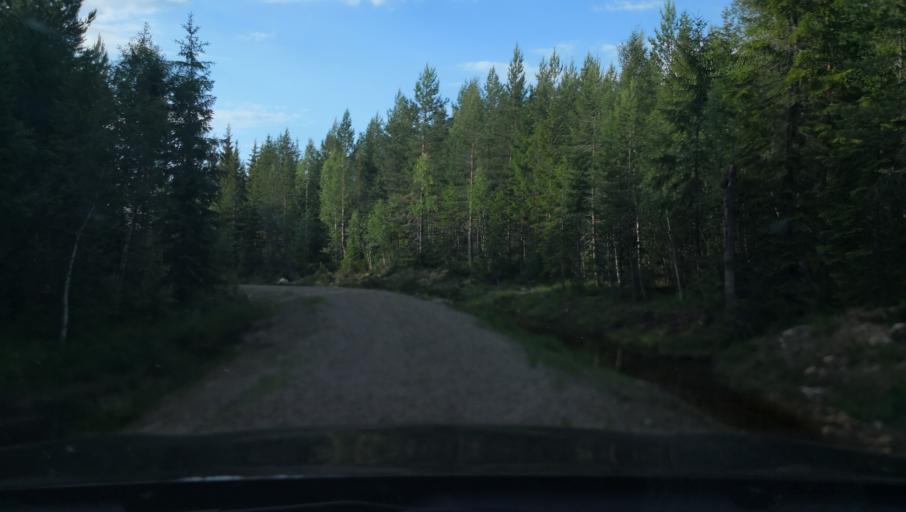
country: SE
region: Dalarna
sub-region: Smedjebackens Kommun
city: Smedjebacken
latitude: 60.0631
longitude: 15.3090
